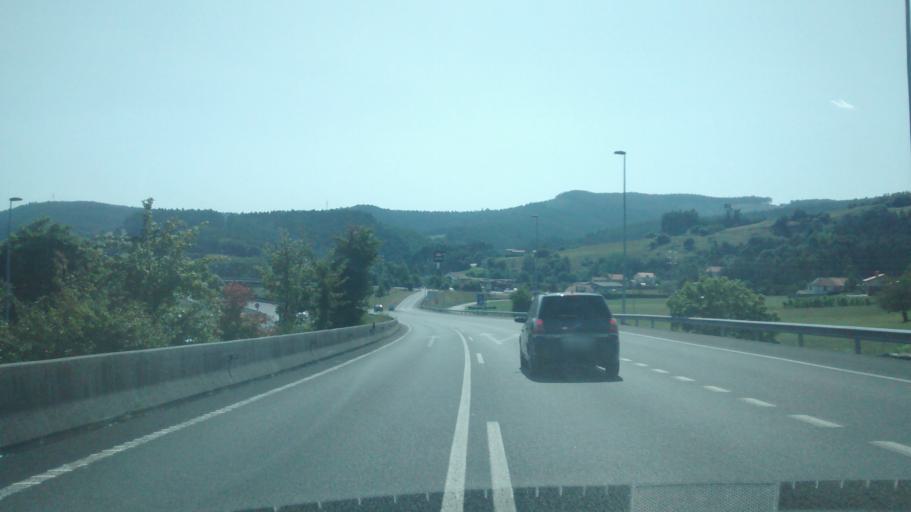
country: ES
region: Cantabria
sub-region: Provincia de Cantabria
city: Barcena de Cicero
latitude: 43.4151
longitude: -3.5474
